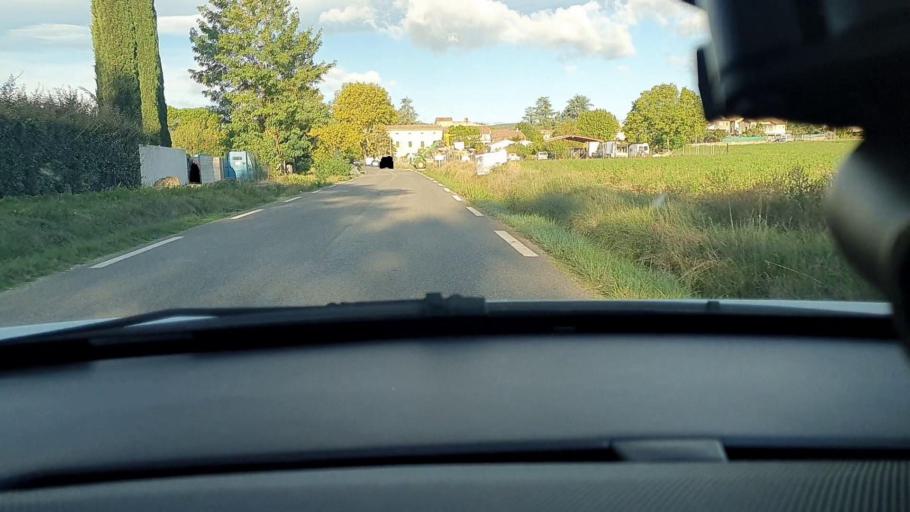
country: FR
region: Languedoc-Roussillon
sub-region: Departement du Gard
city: Saint-Ambroix
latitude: 44.2403
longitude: 4.2260
